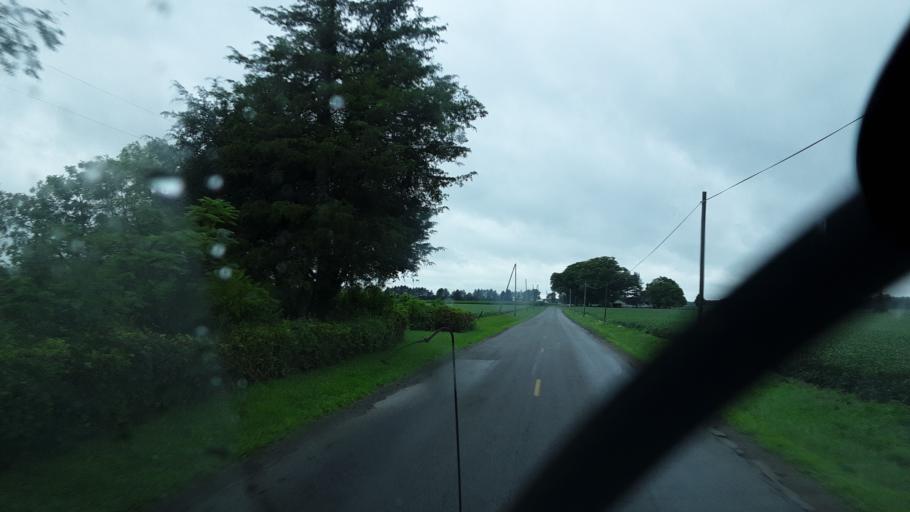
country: US
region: Ohio
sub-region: Van Wert County
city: Van Wert
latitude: 40.8004
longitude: -84.6249
